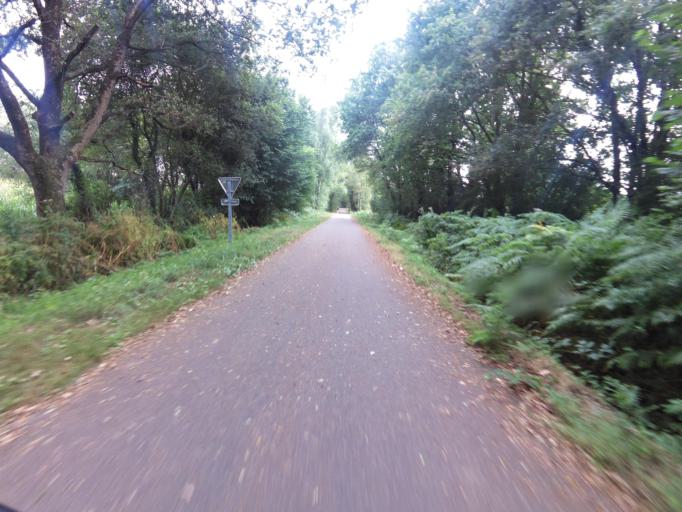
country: FR
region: Brittany
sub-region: Departement du Morbihan
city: Guillac
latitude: 47.8925
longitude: -2.4362
